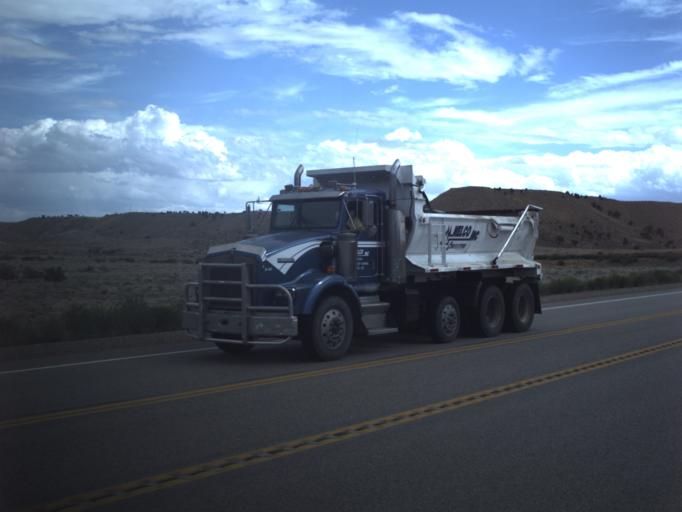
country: US
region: Utah
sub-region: Carbon County
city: Price
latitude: 39.5495
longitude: -110.8159
